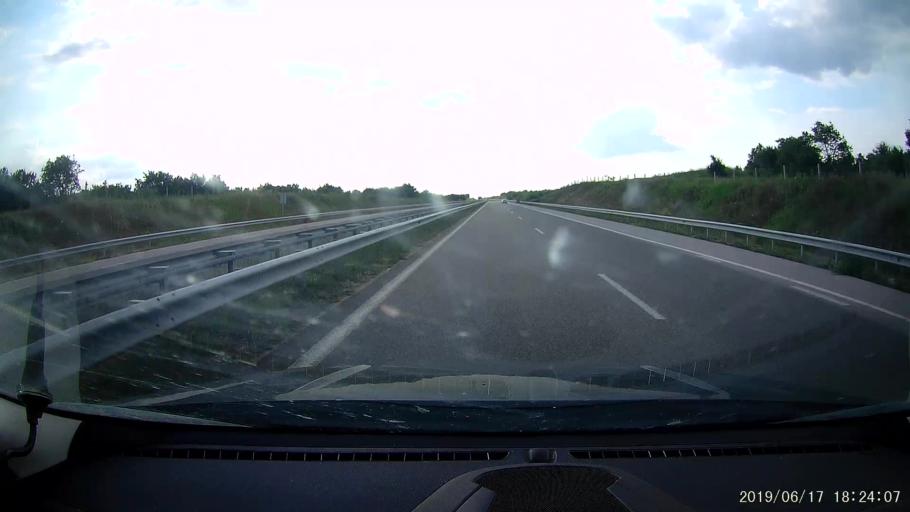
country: BG
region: Khaskovo
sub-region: Obshtina Dimitrovgrad
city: Dimitrovgrad
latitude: 41.9810
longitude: 25.7009
